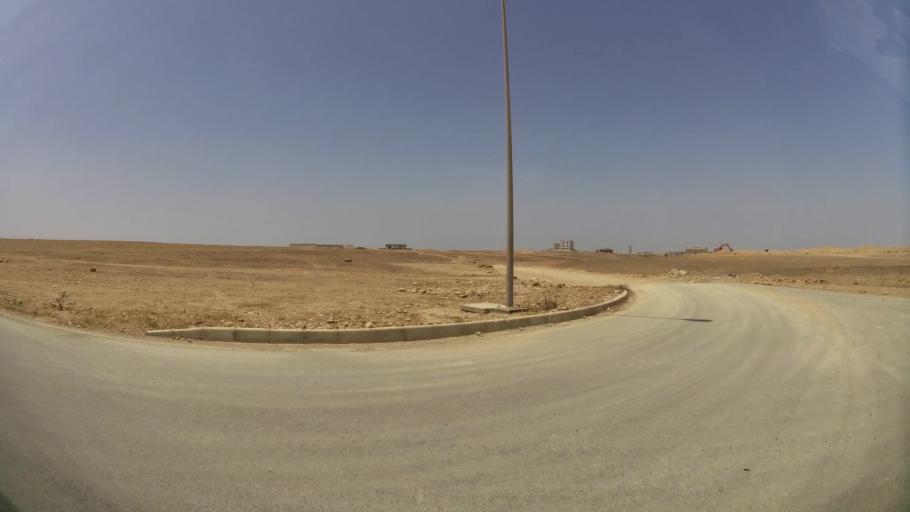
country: OM
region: Zufar
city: Salalah
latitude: 17.0829
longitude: 54.1864
